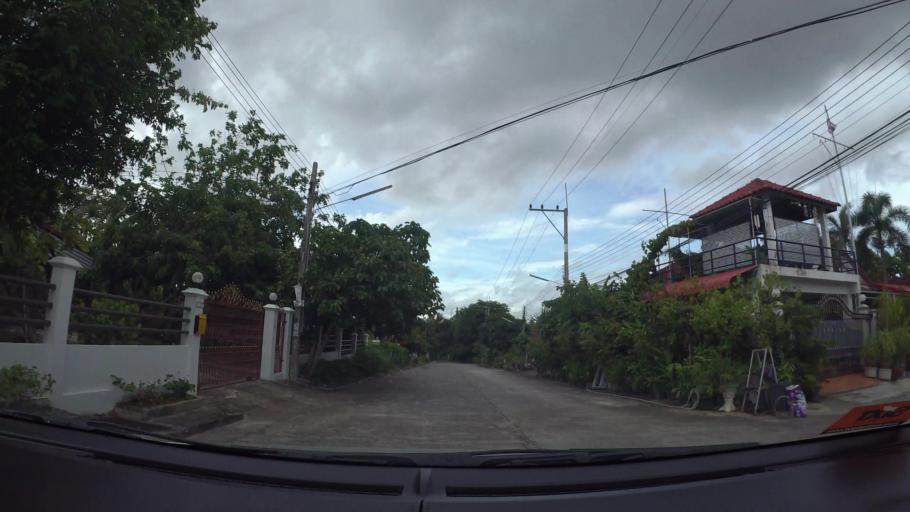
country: TH
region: Chon Buri
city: Sattahip
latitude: 12.7261
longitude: 100.9033
